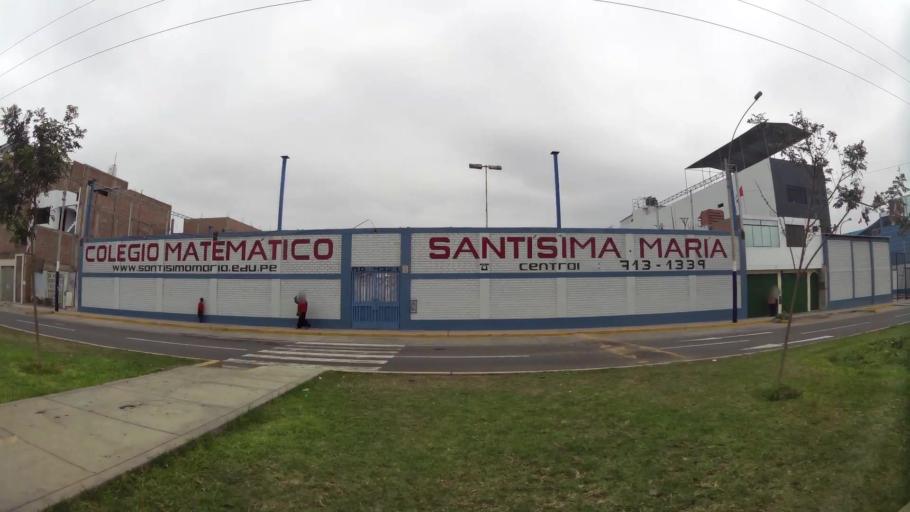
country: PE
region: Lima
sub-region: Lima
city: Surco
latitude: -12.1995
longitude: -77.0075
